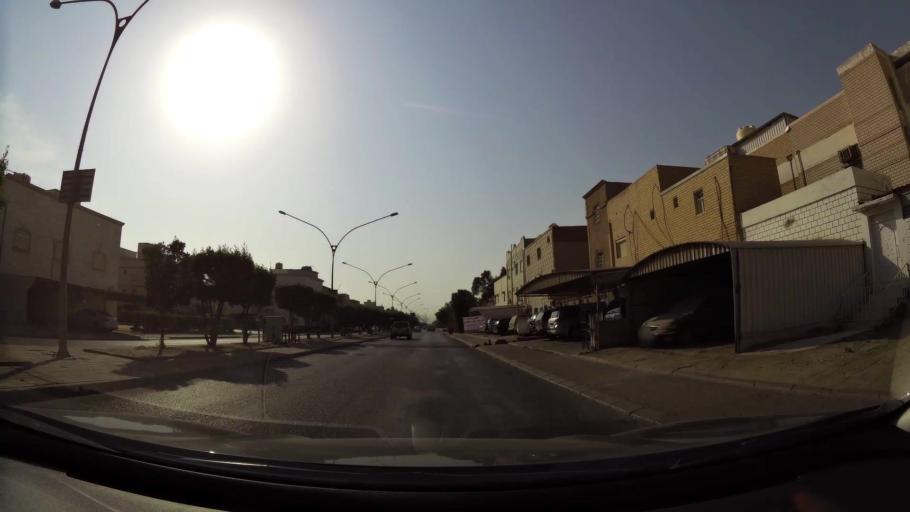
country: KW
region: Al Ahmadi
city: Ar Riqqah
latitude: 29.1611
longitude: 48.0679
